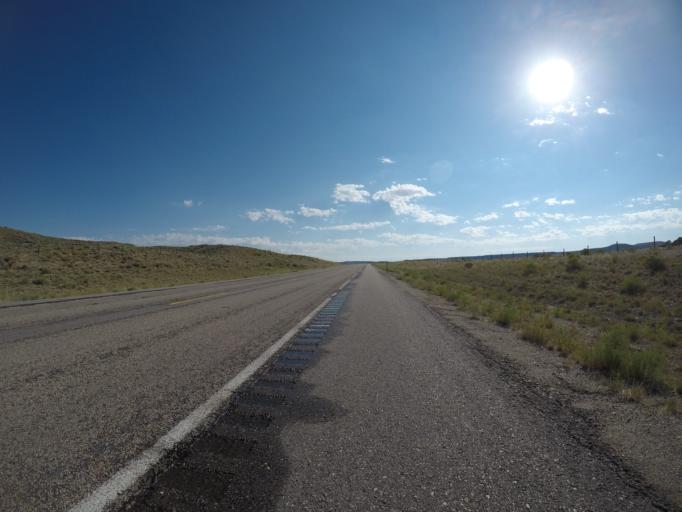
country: US
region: Wyoming
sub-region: Sublette County
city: Marbleton
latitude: 42.0883
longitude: -110.1545
